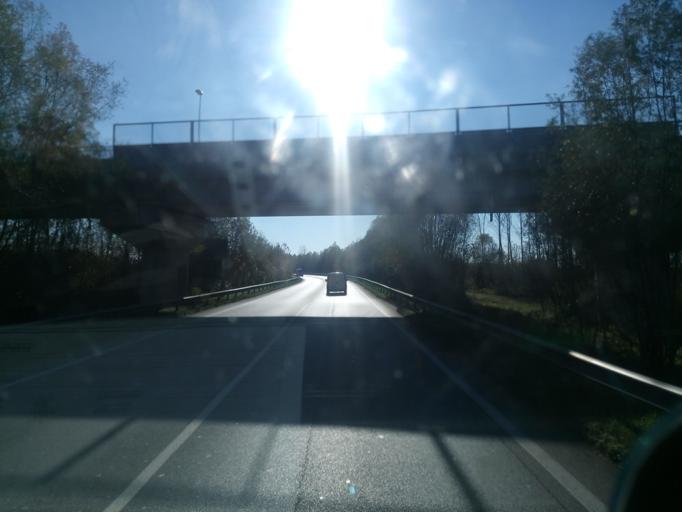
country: IT
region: Veneto
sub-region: Provincia di Padova
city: Mejaniga
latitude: 45.4585
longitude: 11.9216
